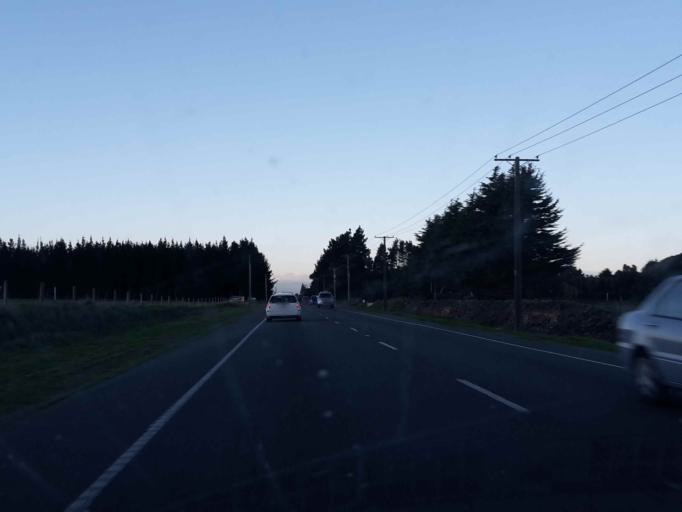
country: NZ
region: Canterbury
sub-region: Selwyn District
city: Prebbleton
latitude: -43.5645
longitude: 172.4508
